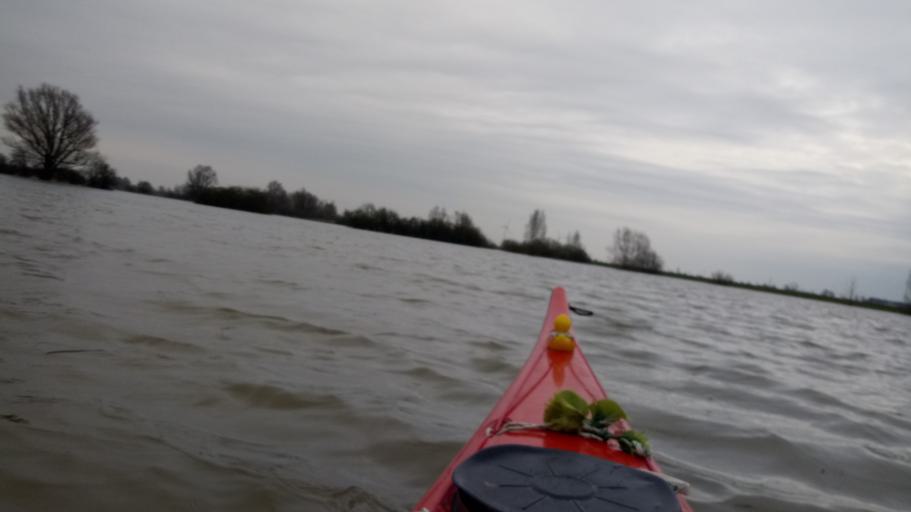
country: NL
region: Gelderland
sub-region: Gemeente Voorst
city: Voorst
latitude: 52.1819
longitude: 6.1700
